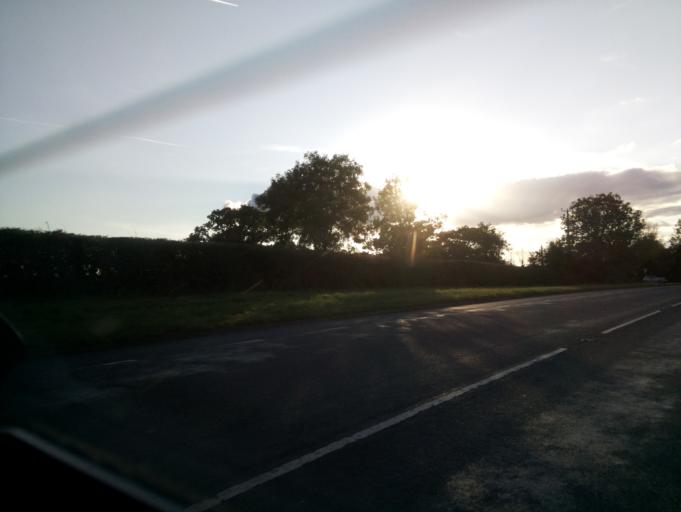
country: GB
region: England
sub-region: Gloucestershire
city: Tewkesbury
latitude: 51.9979
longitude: -2.2213
